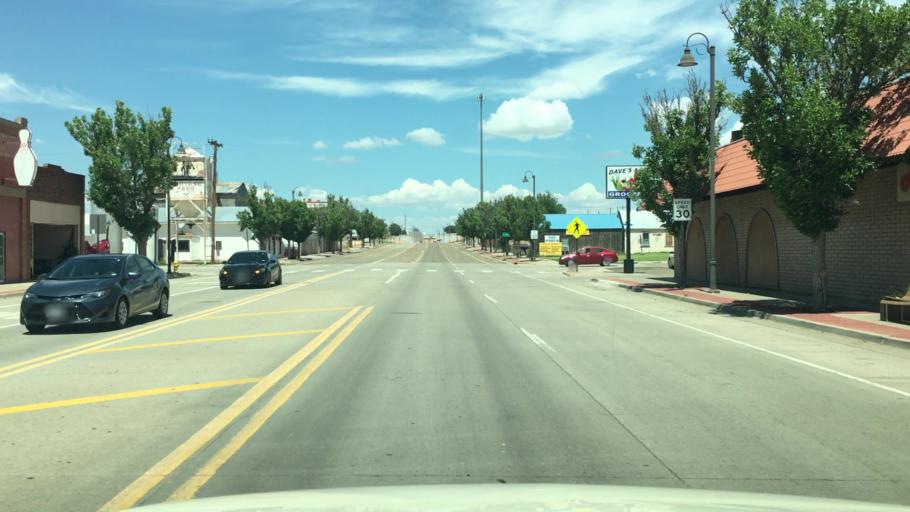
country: US
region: New Mexico
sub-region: De Baca County
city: Fort Sumner
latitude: 34.4722
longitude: -104.2453
